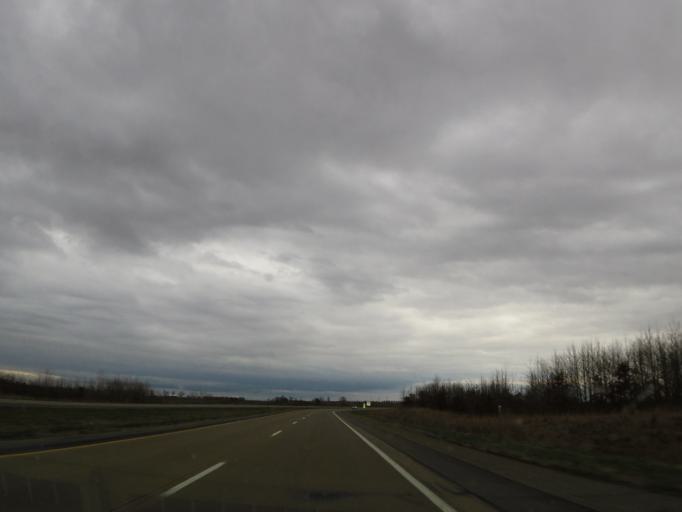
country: US
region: Iowa
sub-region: Henry County
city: Mount Pleasant
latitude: 40.9859
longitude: -91.5230
